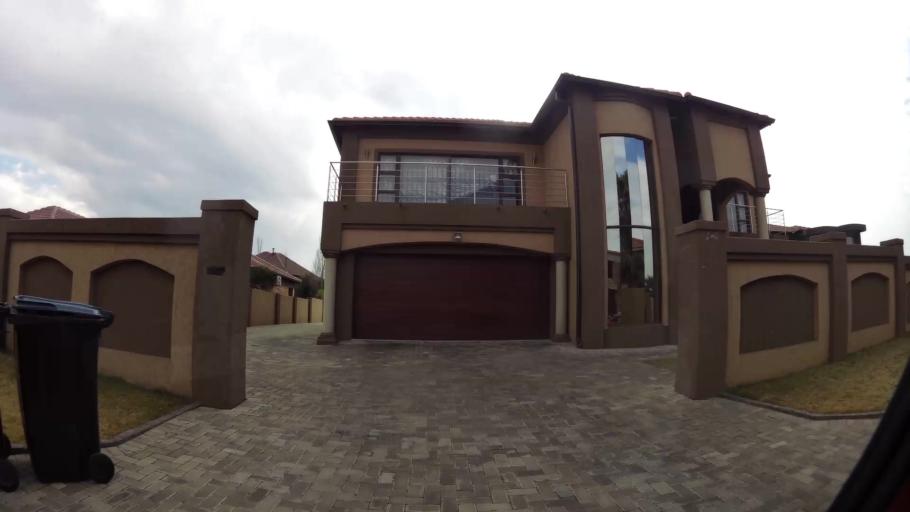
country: ZA
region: Gauteng
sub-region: Sedibeng District Municipality
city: Vanderbijlpark
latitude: -26.7253
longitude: 27.8686
